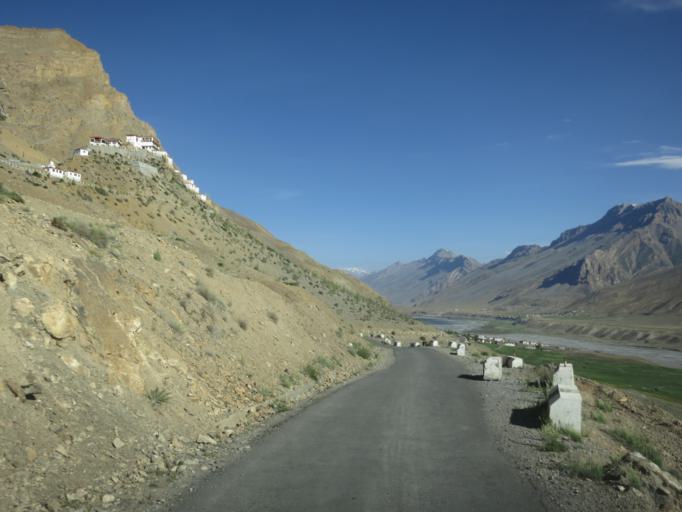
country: IN
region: Himachal Pradesh
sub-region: Shimla
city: Sarahan
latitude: 32.3005
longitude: 78.0075
